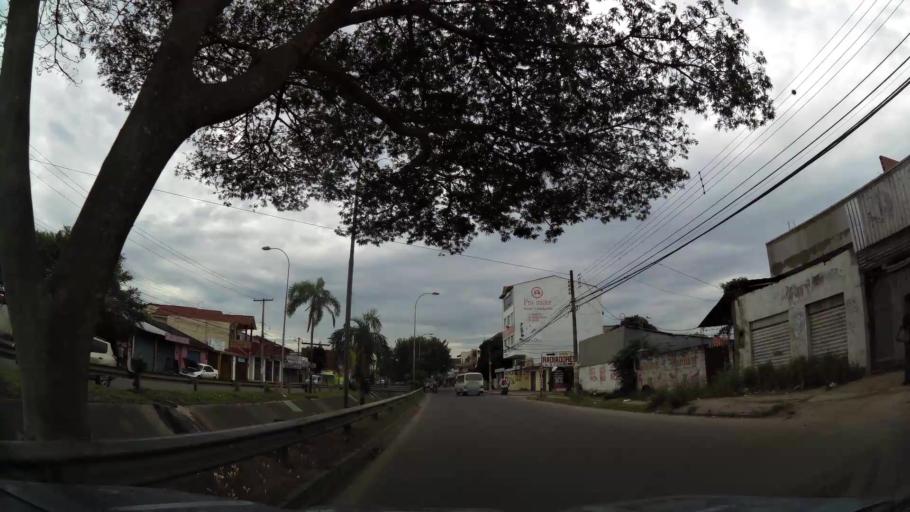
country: BO
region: Santa Cruz
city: Santa Cruz de la Sierra
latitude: -17.7685
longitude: -63.1644
